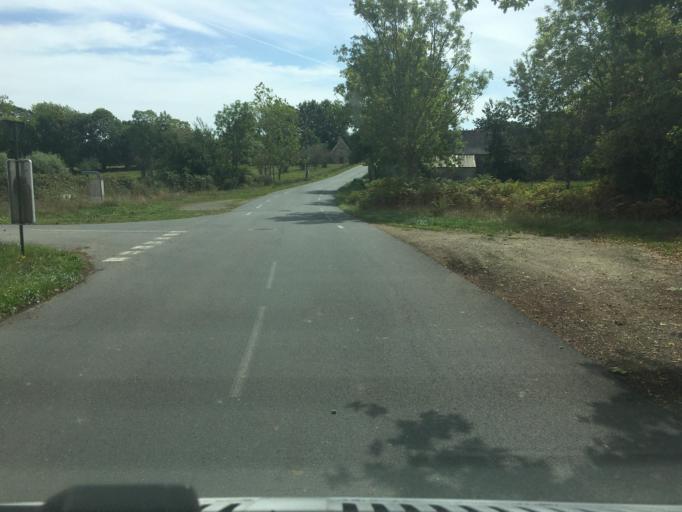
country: FR
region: Brittany
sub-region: Departement du Finistere
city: Loctudy
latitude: 47.8226
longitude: -4.1740
